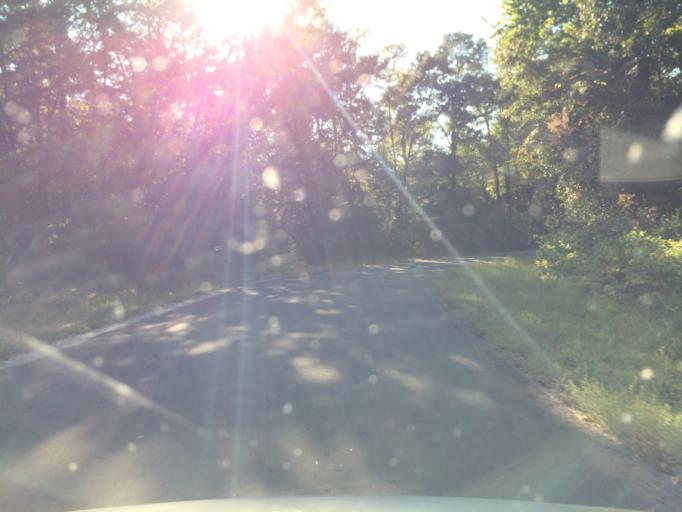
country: US
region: Texas
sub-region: Wood County
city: Hawkins
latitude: 32.6308
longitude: -95.2616
